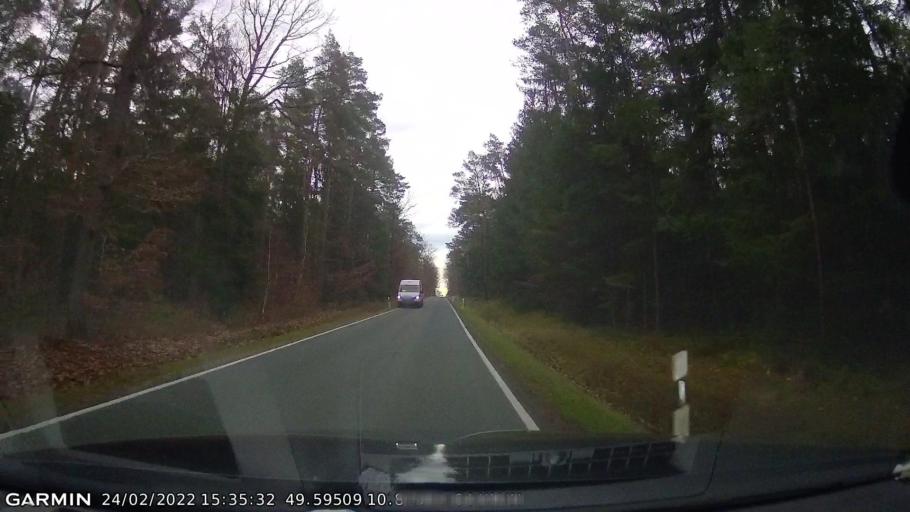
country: DE
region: Bavaria
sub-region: Regierungsbezirk Mittelfranken
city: Herzogenaurach
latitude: 49.5951
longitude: 10.8760
